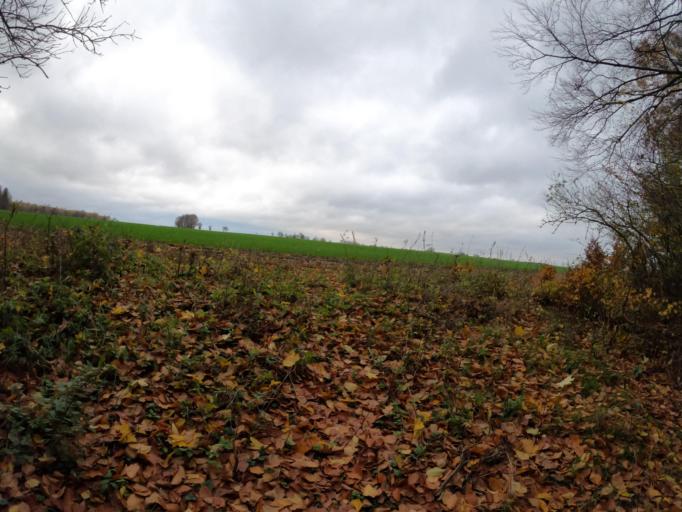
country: PL
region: West Pomeranian Voivodeship
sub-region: Powiat walecki
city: Tuczno
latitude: 53.2527
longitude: 16.2375
